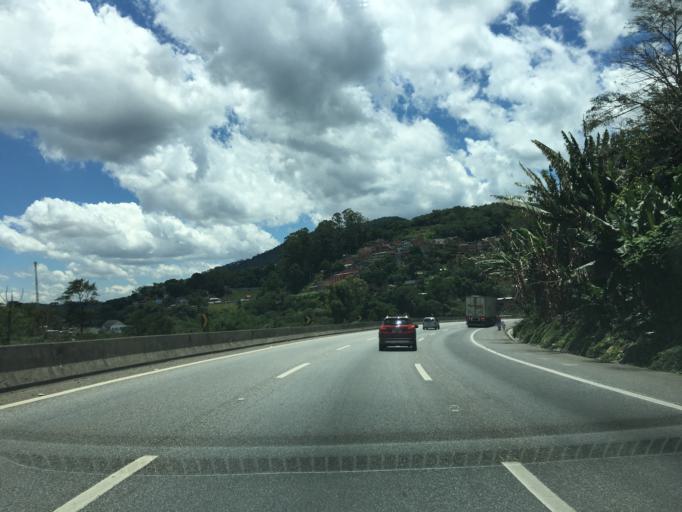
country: BR
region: Sao Paulo
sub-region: Guarulhos
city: Guarulhos
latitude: -23.4043
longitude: -46.5767
